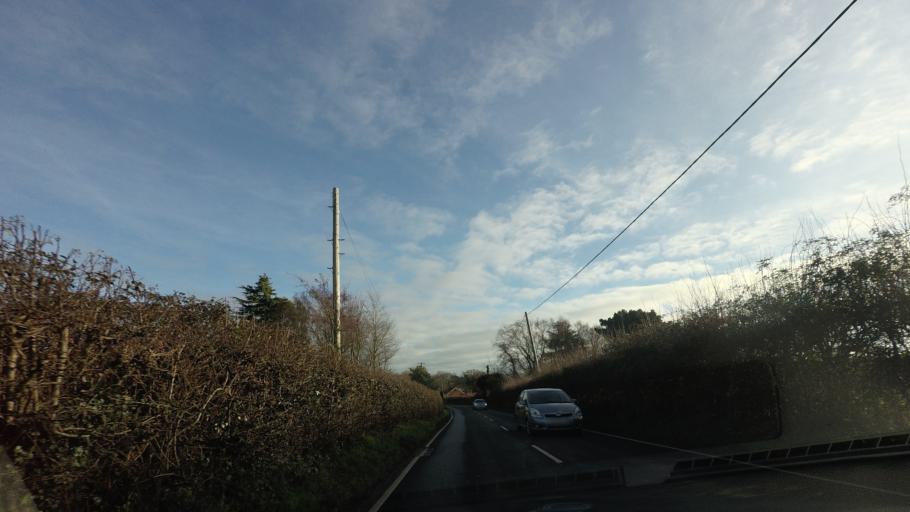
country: GB
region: England
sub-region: East Sussex
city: Bexhill-on-Sea
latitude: 50.8712
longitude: 0.4396
